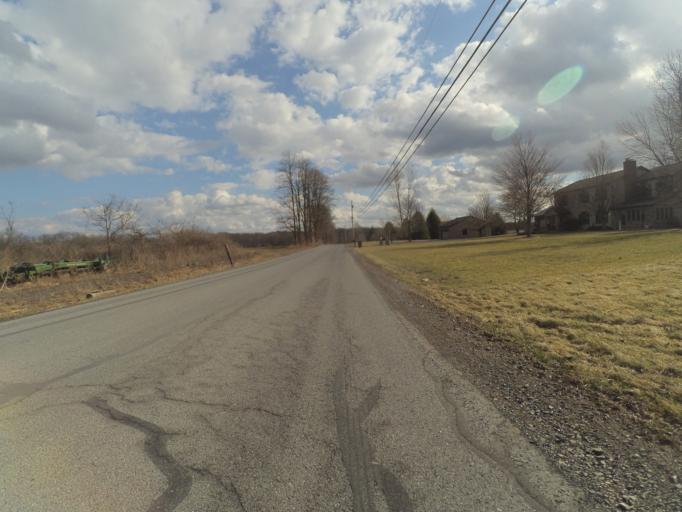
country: US
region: Pennsylvania
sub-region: Centre County
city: Stormstown
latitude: 40.8022
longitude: -77.9914
